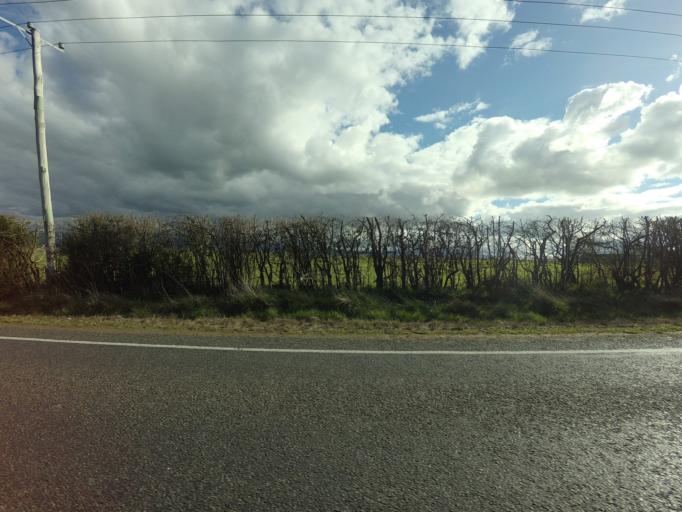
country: AU
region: Tasmania
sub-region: Northern Midlands
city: Longford
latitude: -41.7031
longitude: 147.0772
